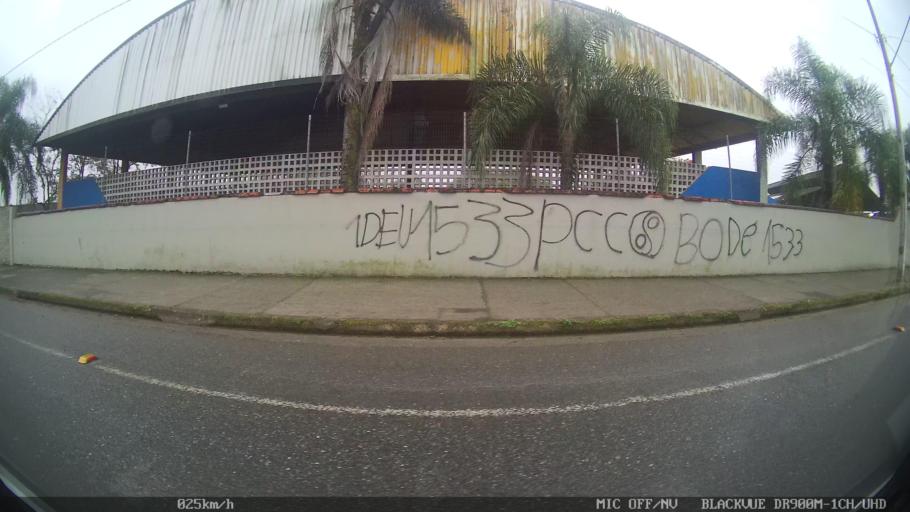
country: BR
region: Santa Catarina
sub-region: Joinville
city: Joinville
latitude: -26.2131
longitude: -48.8245
